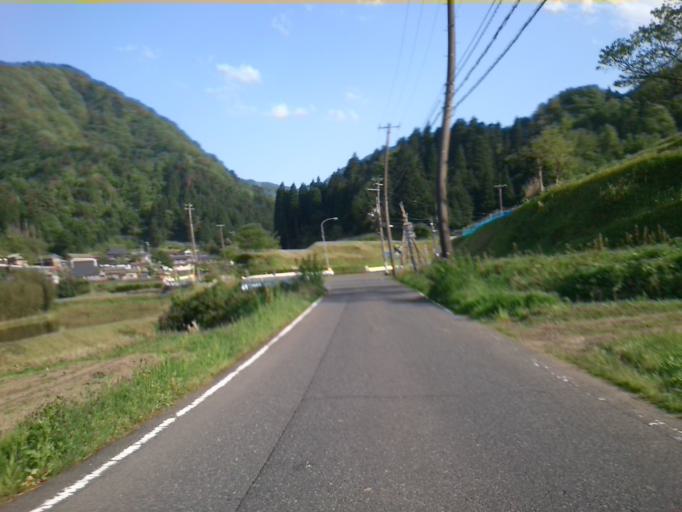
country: JP
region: Kyoto
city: Miyazu
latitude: 35.6815
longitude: 135.1582
